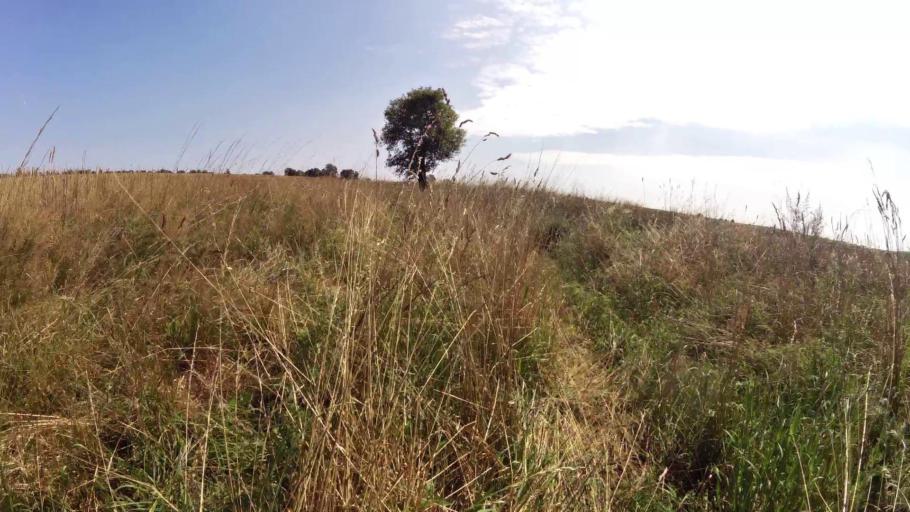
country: PL
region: West Pomeranian Voivodeship
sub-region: Powiat stargardzki
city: Dobrzany
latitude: 53.2822
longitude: 15.4491
